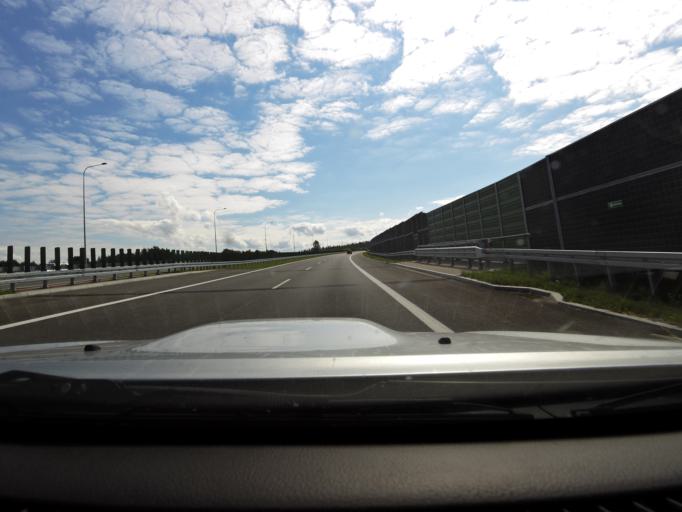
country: PL
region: Warmian-Masurian Voivodeship
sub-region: Powiat ostrodzki
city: Milomlyn
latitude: 53.7700
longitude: 19.8486
